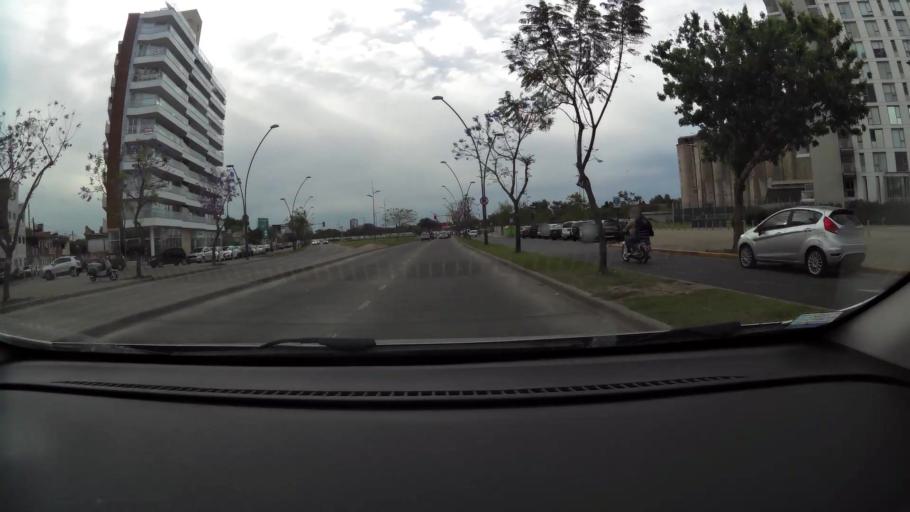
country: AR
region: Santa Fe
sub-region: Departamento de Rosario
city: Rosario
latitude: -32.9229
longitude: -60.6663
